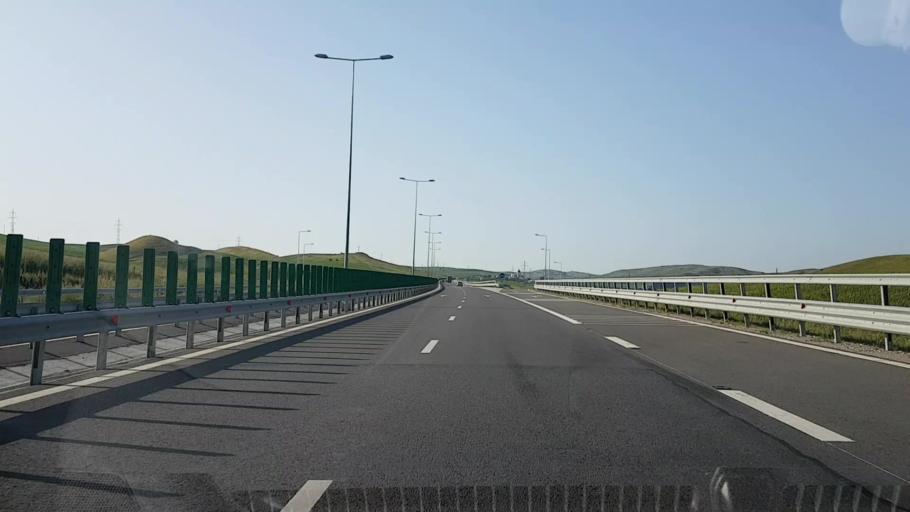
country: RO
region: Alba
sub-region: Comuna Unirea
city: Unirea
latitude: 46.4183
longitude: 23.7986
